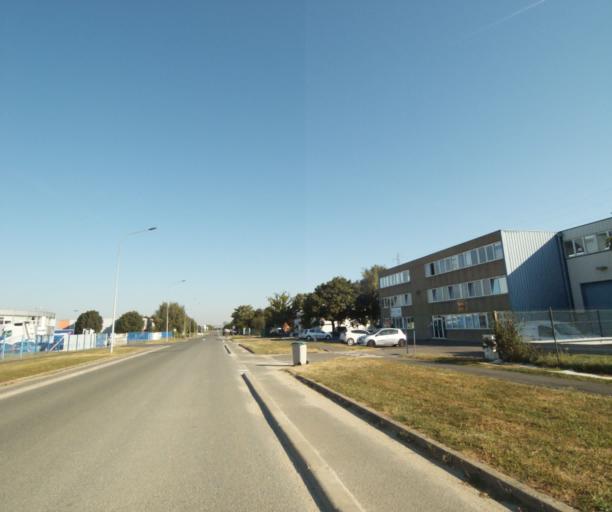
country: FR
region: Ile-de-France
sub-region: Departement de Seine-et-Marne
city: Lieusaint
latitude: 48.6207
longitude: 2.5689
